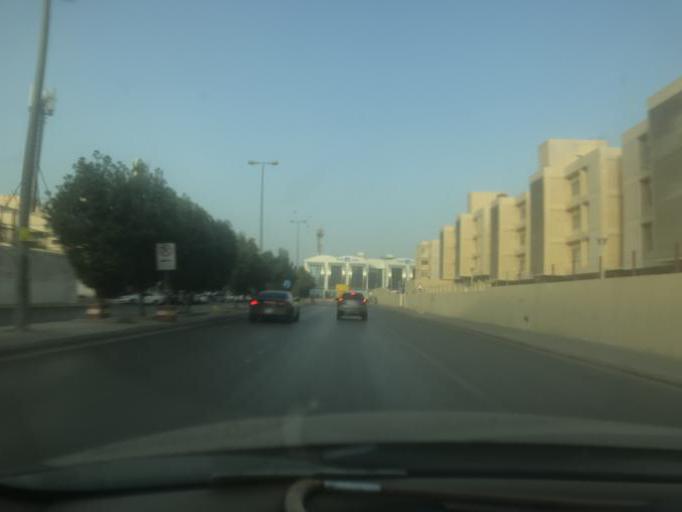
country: SA
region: Ar Riyad
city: Riyadh
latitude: 24.7104
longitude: 46.6832
